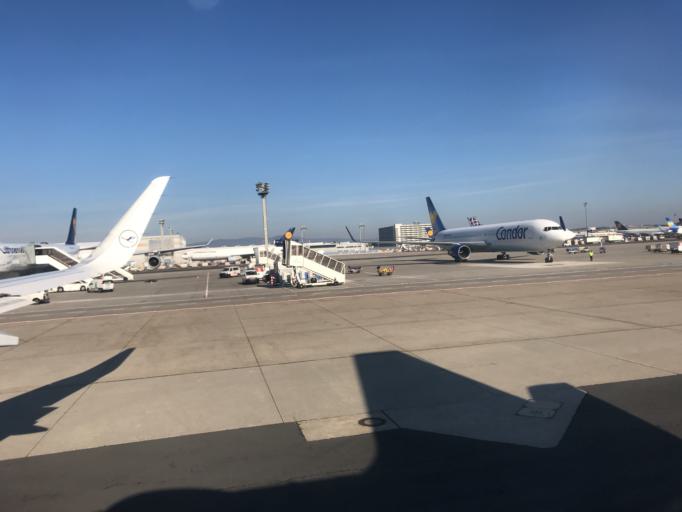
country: DE
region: Hesse
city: Kelsterbach
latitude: 50.0375
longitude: 8.5469
